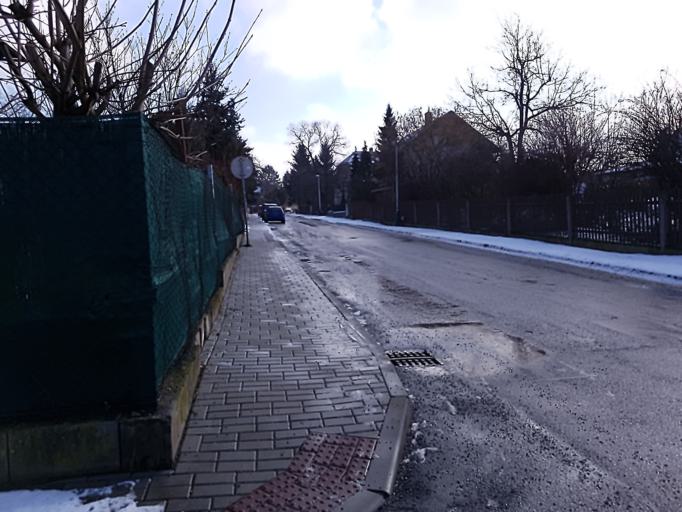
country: CZ
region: Central Bohemia
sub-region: Okres Praha-Vychod
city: Ricany
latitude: 49.9995
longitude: 14.6728
